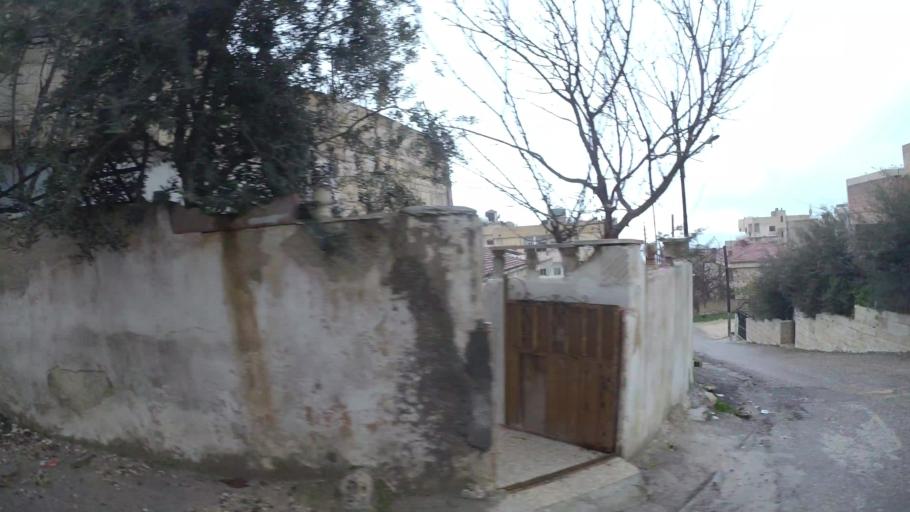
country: JO
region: Amman
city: Al Jubayhah
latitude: 32.0331
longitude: 35.8367
